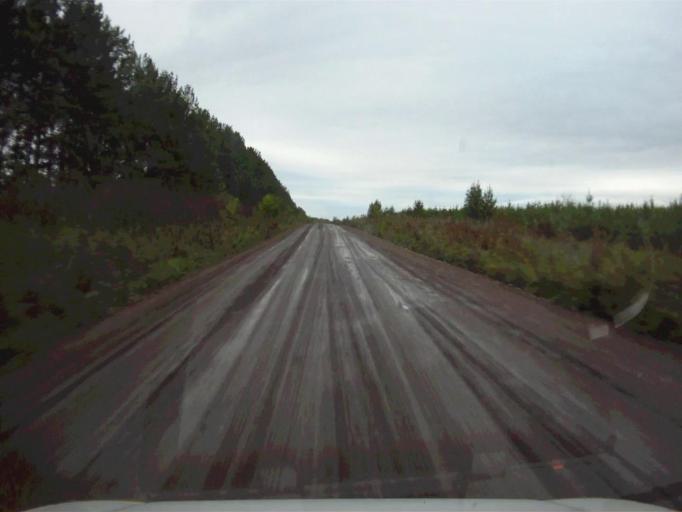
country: RU
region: Chelyabinsk
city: Nyazepetrovsk
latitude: 56.1447
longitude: 59.2838
